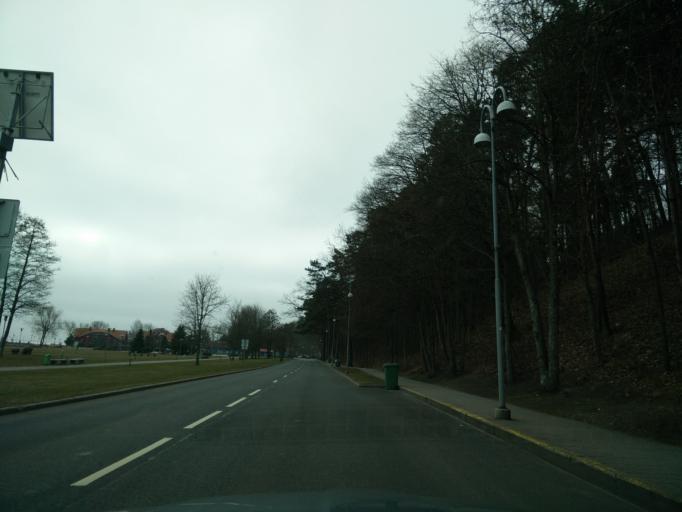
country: LT
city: Neringa
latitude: 55.5356
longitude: 21.1176
